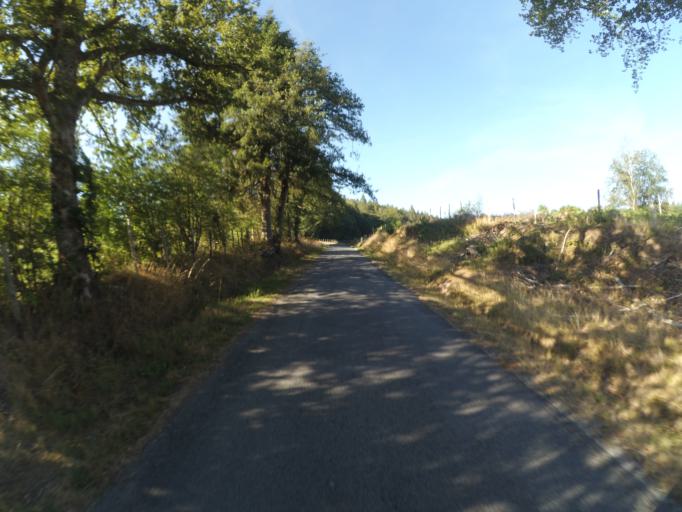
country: FR
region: Limousin
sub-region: Departement de la Creuse
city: Banize
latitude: 45.7452
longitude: 2.0294
